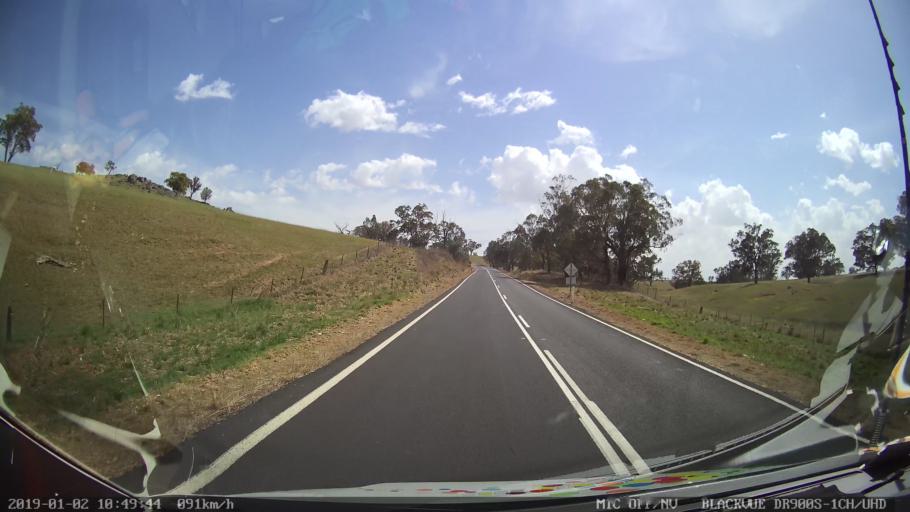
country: AU
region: New South Wales
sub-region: Cootamundra
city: Cootamundra
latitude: -34.7207
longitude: 148.2762
